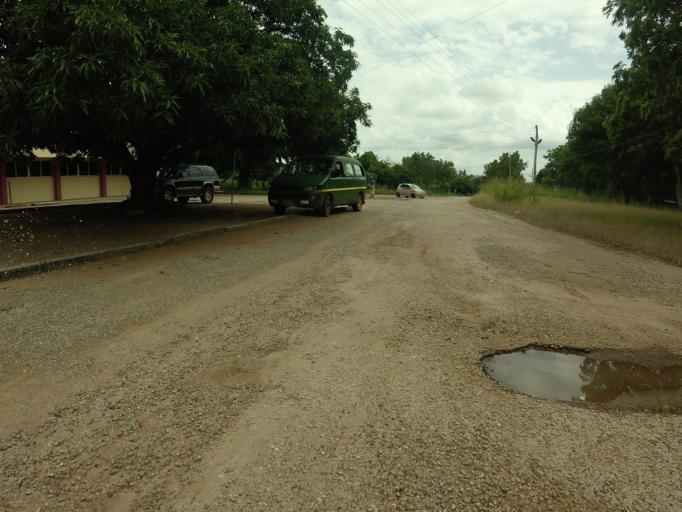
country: GH
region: Volta
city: Ho
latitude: 6.5959
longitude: 0.4643
